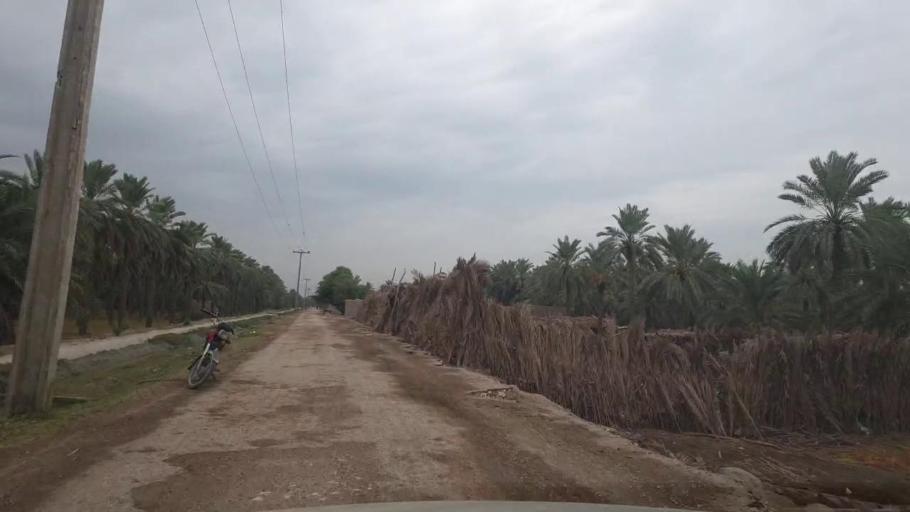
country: PK
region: Sindh
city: Khairpur
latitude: 27.6071
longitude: 68.8166
